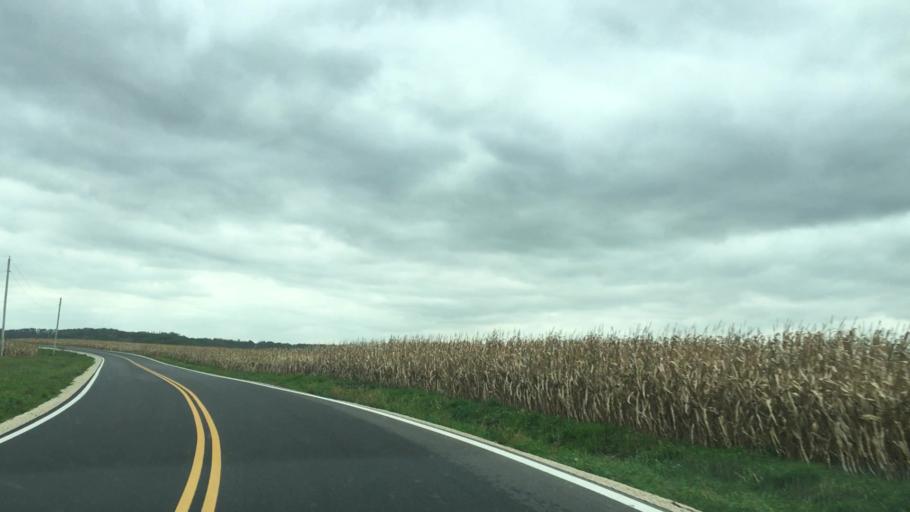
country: US
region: Minnesota
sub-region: Fillmore County
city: Preston
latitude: 43.7580
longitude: -92.0209
